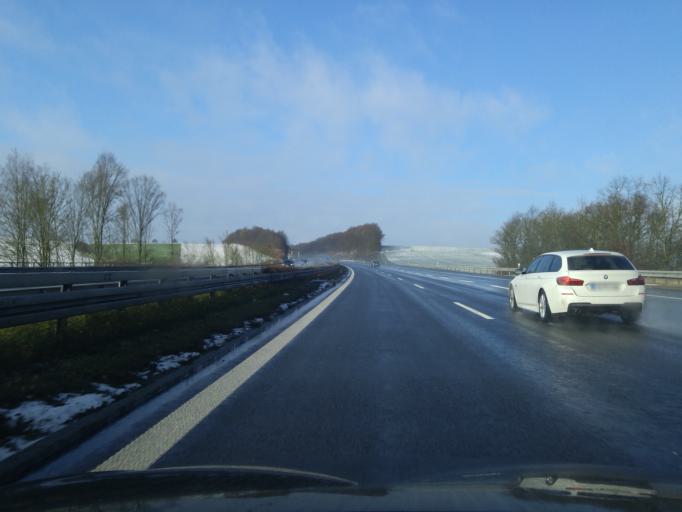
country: DE
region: Bavaria
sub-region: Regierungsbezirk Unterfranken
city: Wasserlosen
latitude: 50.0671
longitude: 10.0436
